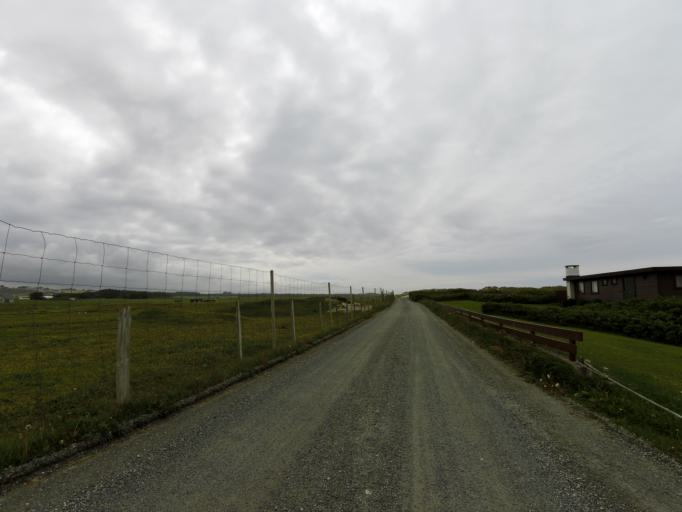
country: NO
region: Rogaland
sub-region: Klepp
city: Kleppe
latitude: 58.8015
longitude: 5.5520
